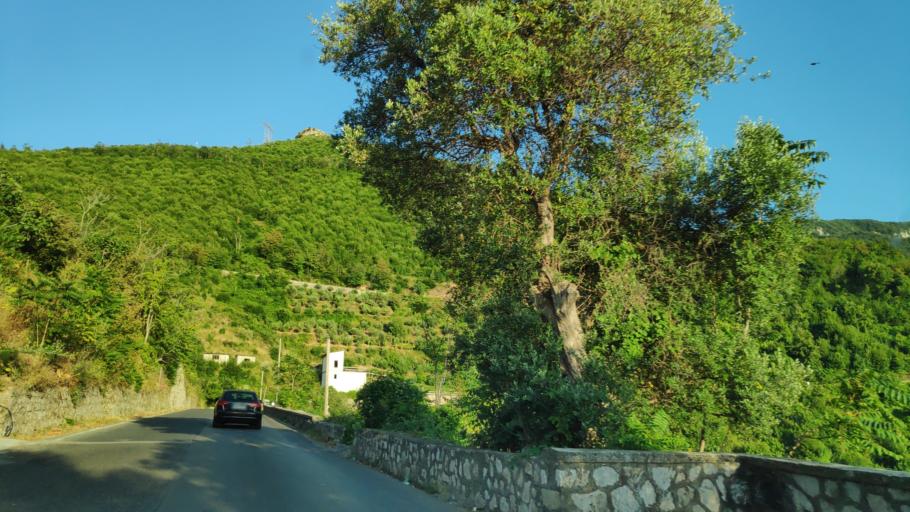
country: IT
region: Campania
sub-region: Provincia di Salerno
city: Corbara
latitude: 40.7219
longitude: 14.5996
